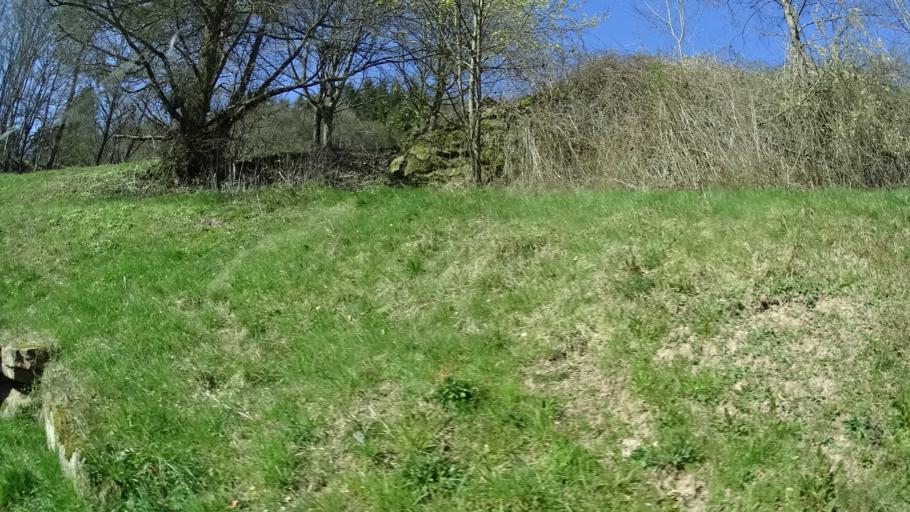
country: DE
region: Hesse
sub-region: Regierungsbezirk Darmstadt
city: Rothenberg
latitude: 49.5359
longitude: 8.9185
